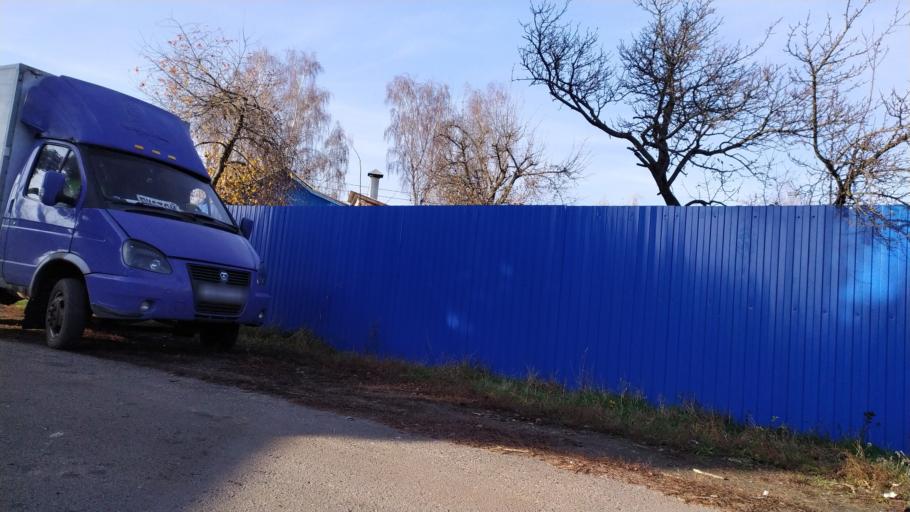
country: RU
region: Kursk
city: Kursk
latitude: 51.6444
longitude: 36.1404
